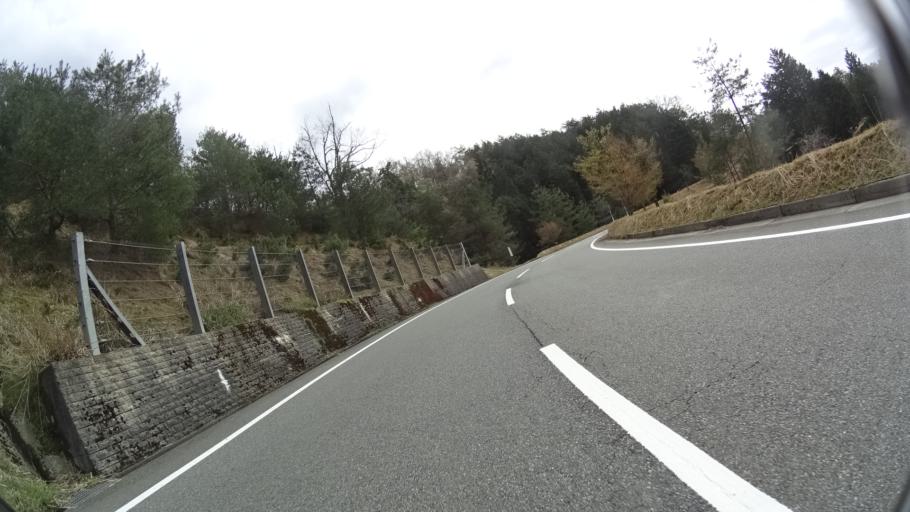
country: JP
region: Hyogo
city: Toyooka
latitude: 35.5070
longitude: 134.9018
